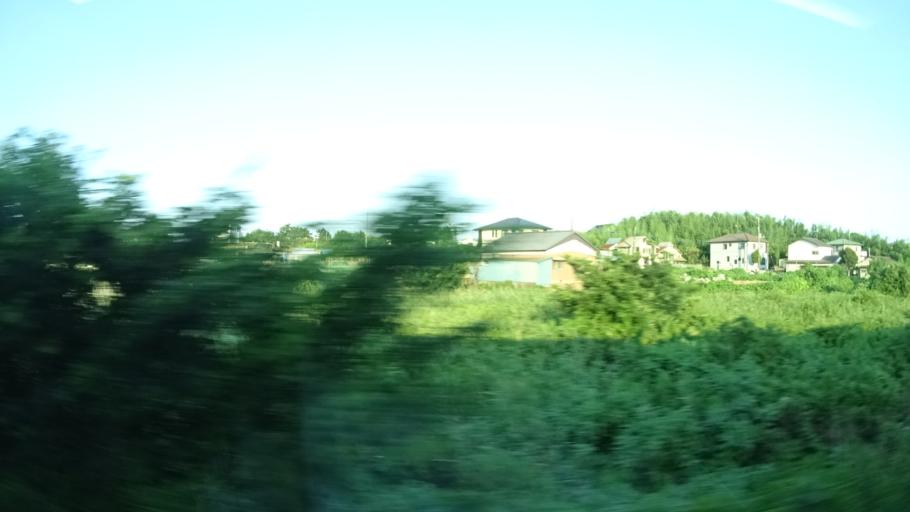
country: JP
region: Ibaraki
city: Ishioka
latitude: 36.1995
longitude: 140.2778
